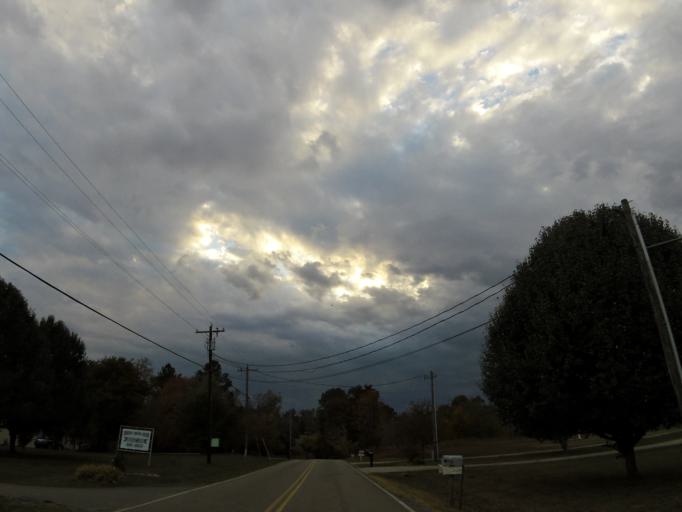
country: US
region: Tennessee
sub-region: Blount County
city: Louisville
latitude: 35.7823
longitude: -84.0750
